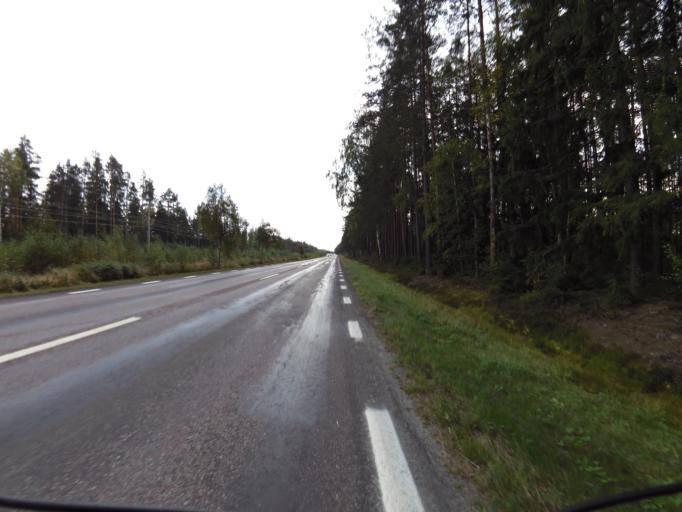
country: SE
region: Gaevleborg
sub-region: Ockelbo Kommun
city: Ockelbo
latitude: 60.8593
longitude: 16.7000
